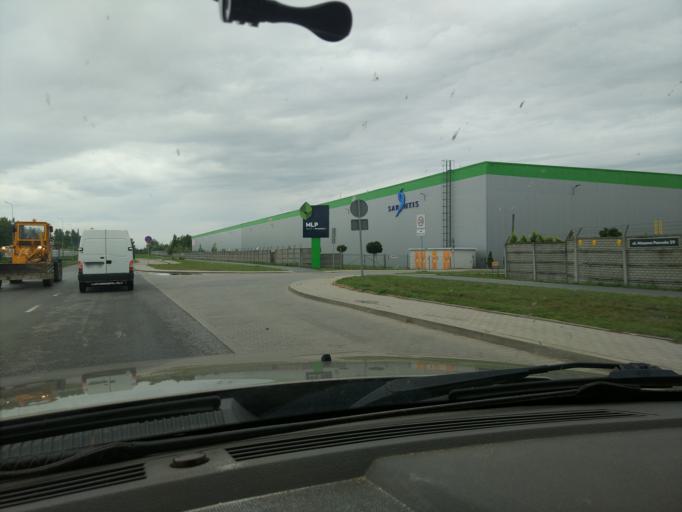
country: PL
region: Masovian Voivodeship
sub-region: Powiat pruszkowski
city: Brwinow
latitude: 52.1777
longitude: 20.7501
